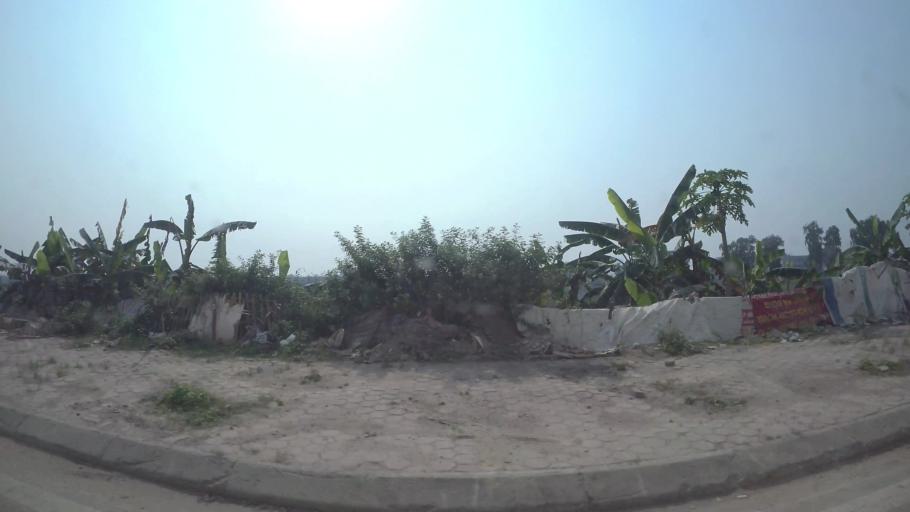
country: VN
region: Ha Noi
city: Ha Dong
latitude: 20.9446
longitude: 105.7893
